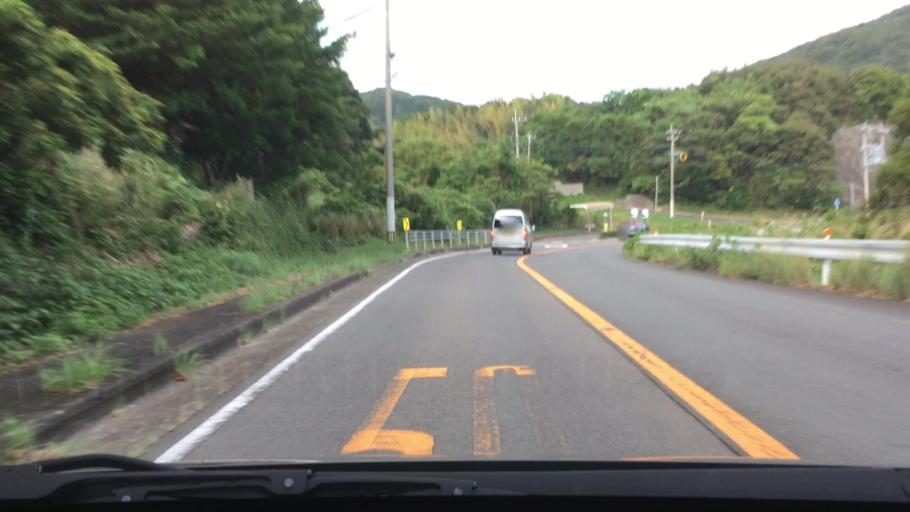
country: JP
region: Nagasaki
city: Togitsu
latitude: 32.8216
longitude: 129.7295
